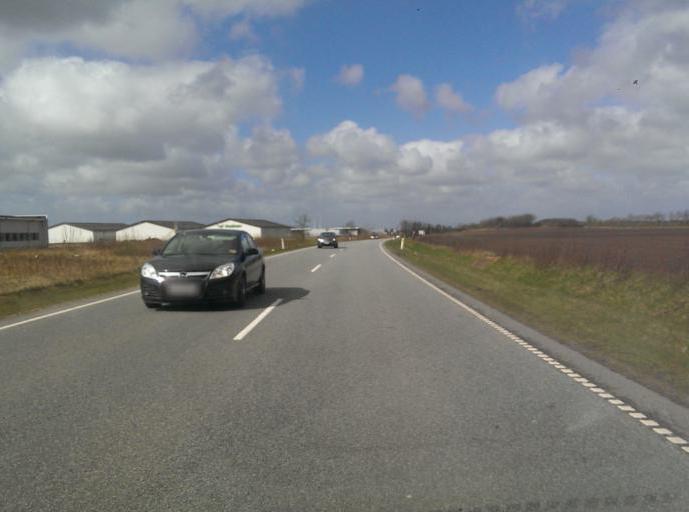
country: DK
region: South Denmark
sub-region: Esbjerg Kommune
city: Esbjerg
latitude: 55.5165
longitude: 8.4787
